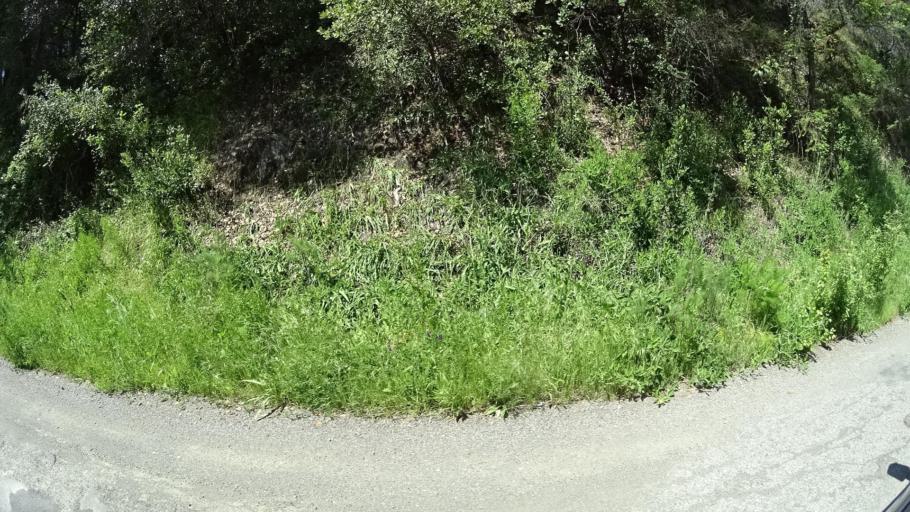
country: US
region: California
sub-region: Humboldt County
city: Redway
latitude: 40.1704
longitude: -123.6046
